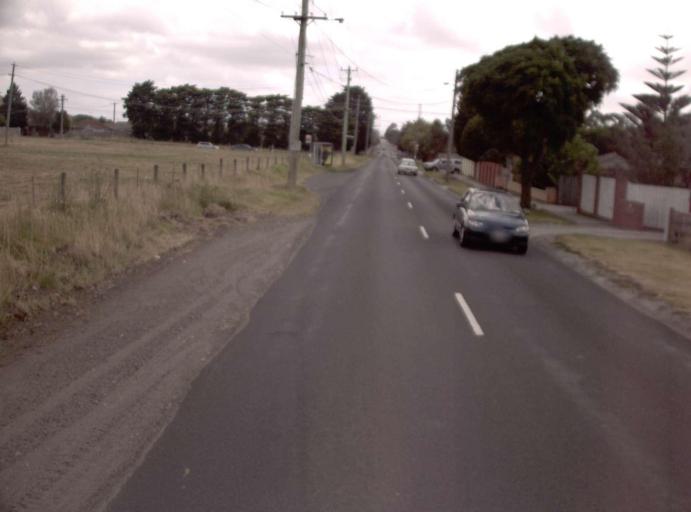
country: AU
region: Victoria
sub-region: Monash
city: Oakleigh South
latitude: -37.9438
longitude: 145.0973
